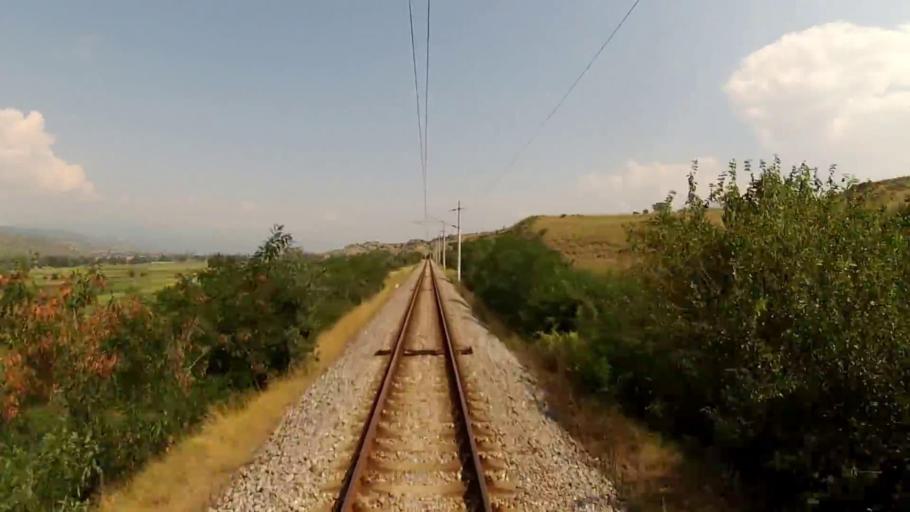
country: BG
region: Blagoevgrad
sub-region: Obshtina Sandanski
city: Sandanski
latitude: 41.5859
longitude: 23.2378
